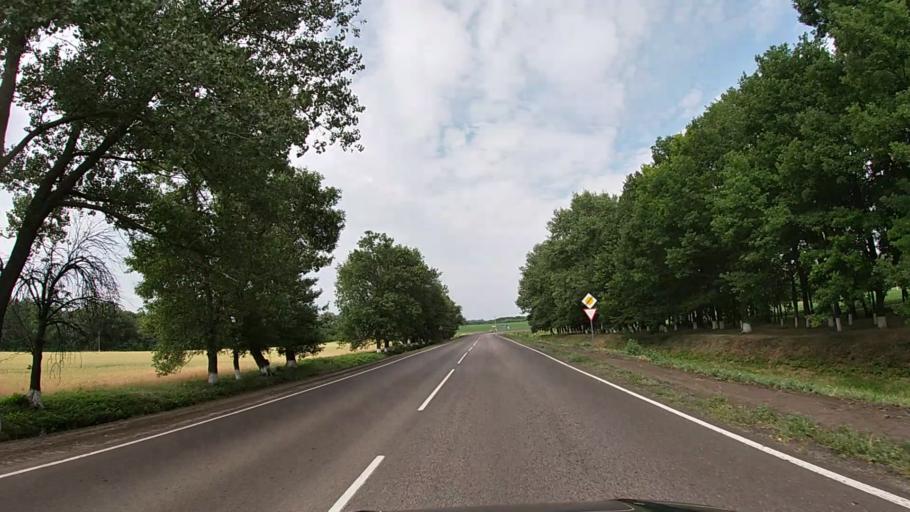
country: RU
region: Belgorod
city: Krasnaya Yaruga
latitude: 50.8095
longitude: 35.5033
